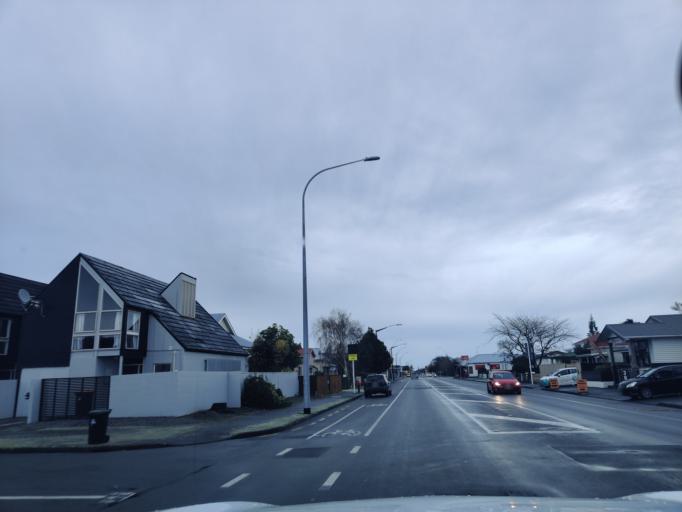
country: NZ
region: Manawatu-Wanganui
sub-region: Palmerston North City
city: Palmerston North
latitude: -40.3472
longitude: 175.6122
